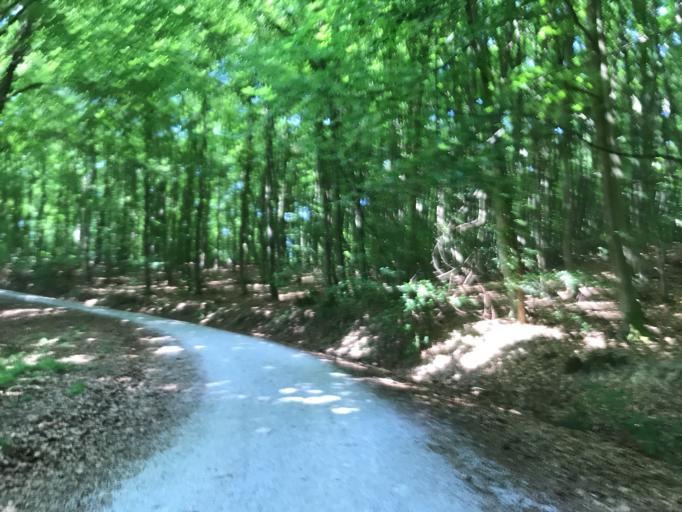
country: DE
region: Hesse
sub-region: Regierungsbezirk Darmstadt
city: Walluf
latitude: 50.0802
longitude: 8.1862
